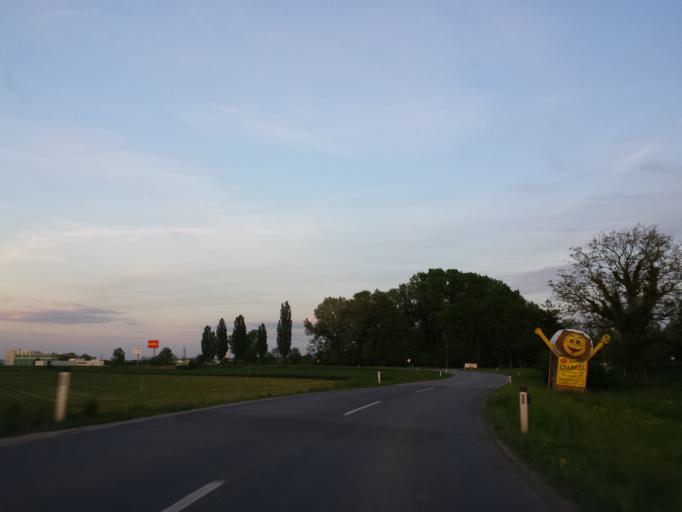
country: AT
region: Lower Austria
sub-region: Politischer Bezirk Tulln
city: Langenrohr
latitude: 48.3194
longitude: 16.0112
